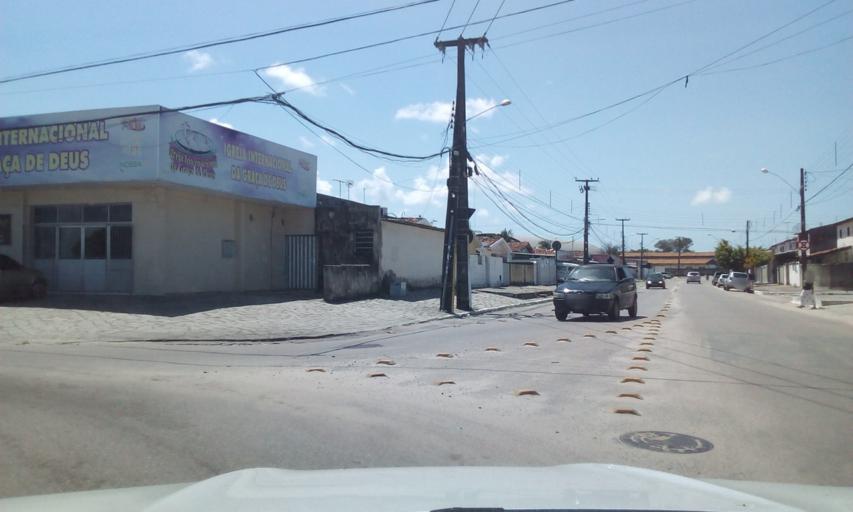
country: BR
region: Paraiba
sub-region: Conde
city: Conde
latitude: -7.2049
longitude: -34.8466
